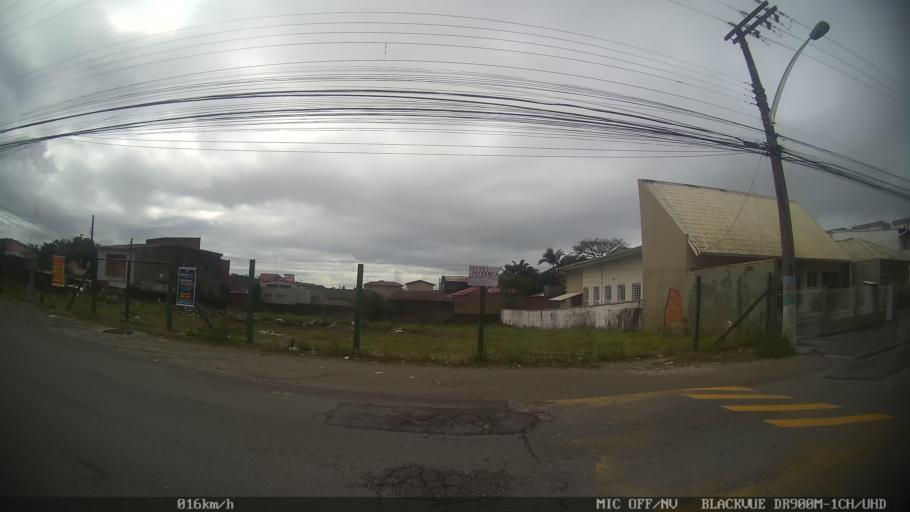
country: BR
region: Santa Catarina
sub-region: Biguacu
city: Biguacu
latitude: -27.5336
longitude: -48.6405
